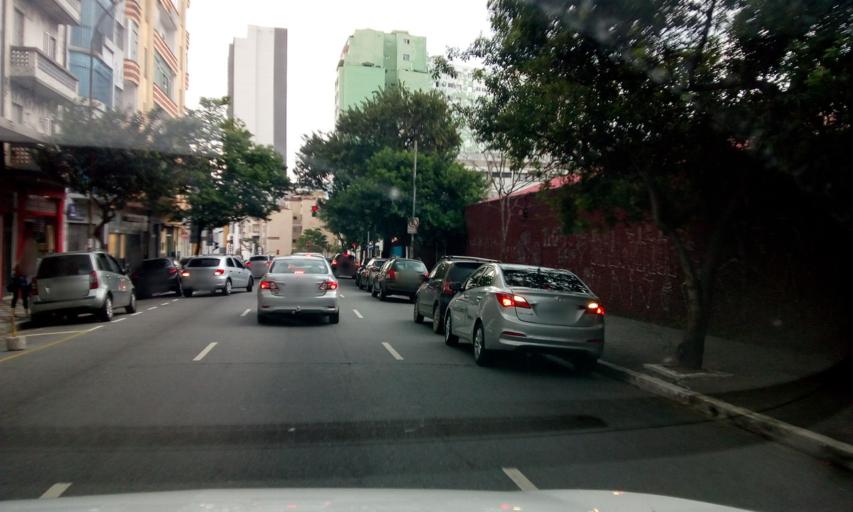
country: BR
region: Sao Paulo
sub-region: Sao Paulo
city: Sao Paulo
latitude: -23.5526
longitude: -46.6312
